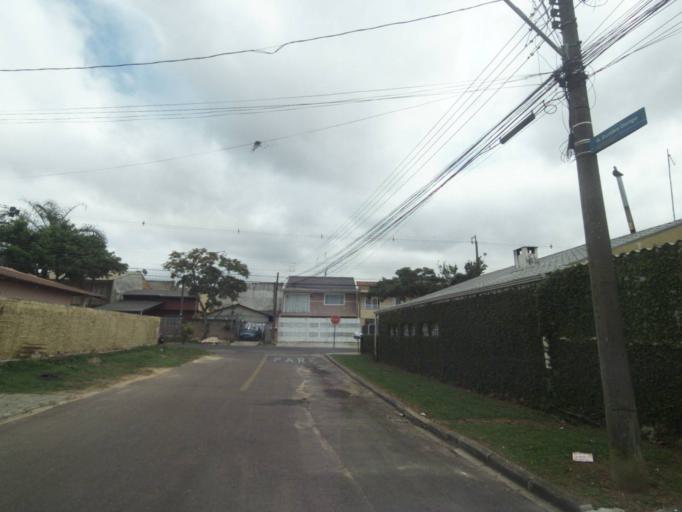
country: BR
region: Parana
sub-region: Sao Jose Dos Pinhais
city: Sao Jose dos Pinhais
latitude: -25.5464
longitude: -49.2542
